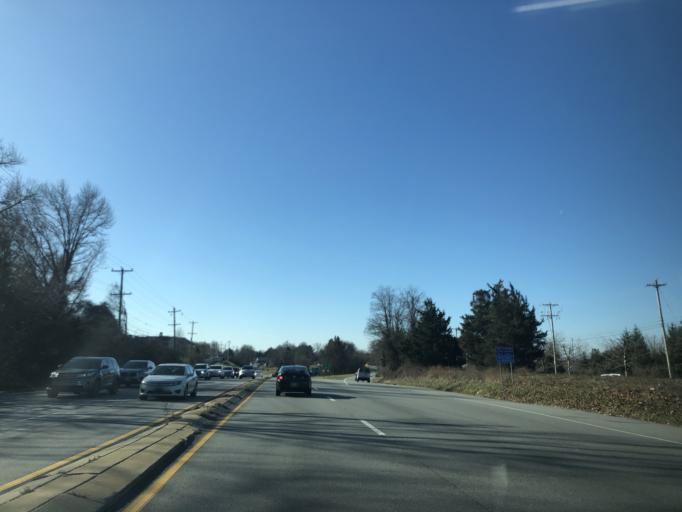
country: US
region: Pennsylvania
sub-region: Chester County
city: Kennett Square
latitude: 39.8594
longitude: -75.6880
